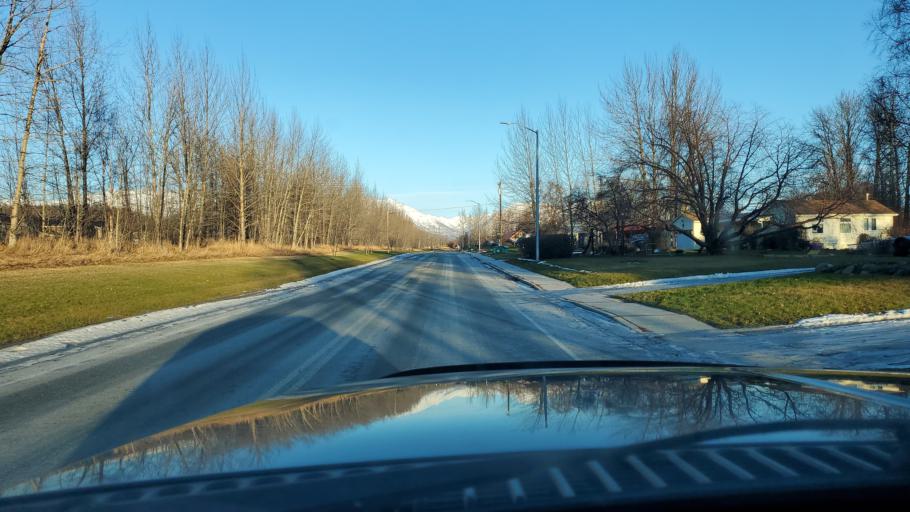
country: US
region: Alaska
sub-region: Matanuska-Susitna Borough
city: Palmer
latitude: 61.6099
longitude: -149.1086
